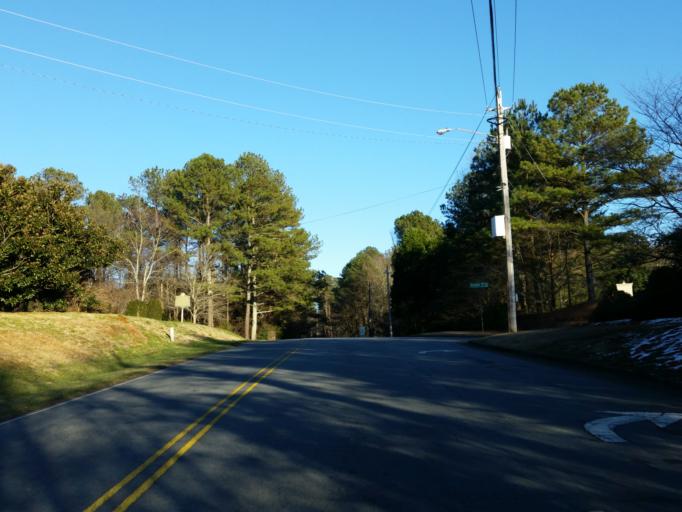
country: US
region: Georgia
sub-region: Cobb County
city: Marietta
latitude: 33.9639
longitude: -84.6080
